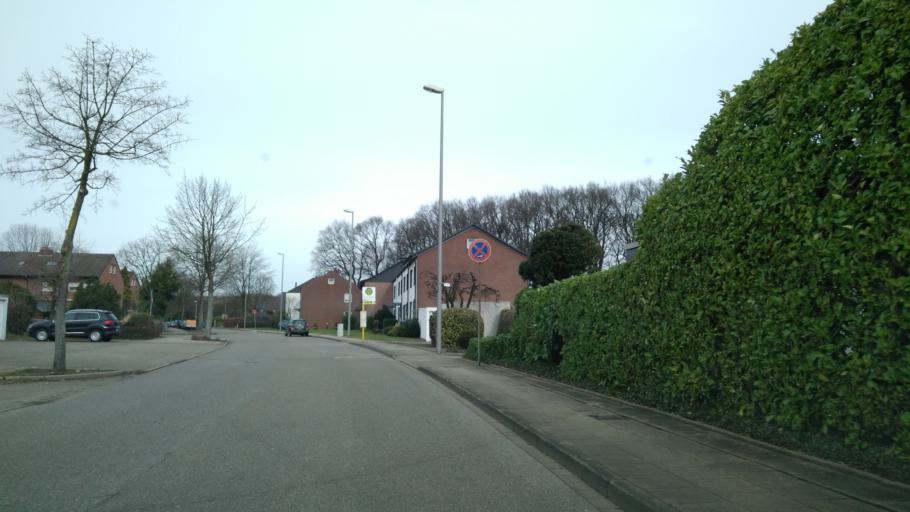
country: DE
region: North Rhine-Westphalia
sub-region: Regierungsbezirk Munster
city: Gladbeck
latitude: 51.5819
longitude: 6.9703
